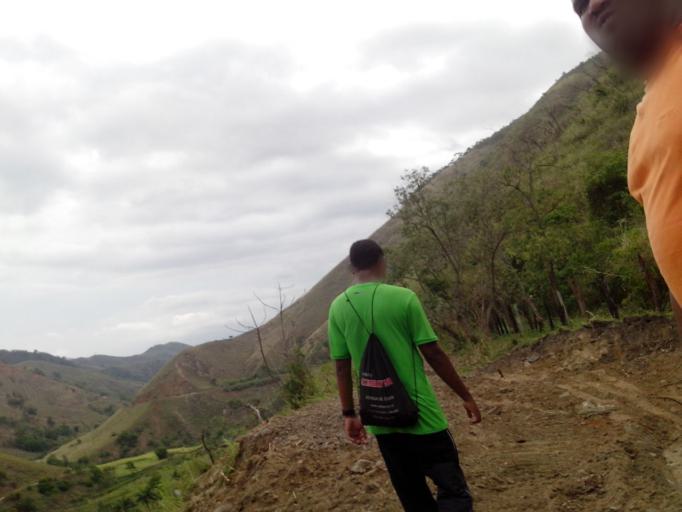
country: BR
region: Rio de Janeiro
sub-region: Miguel Pereira
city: Miguel Pereira
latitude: -22.4984
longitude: -43.4946
